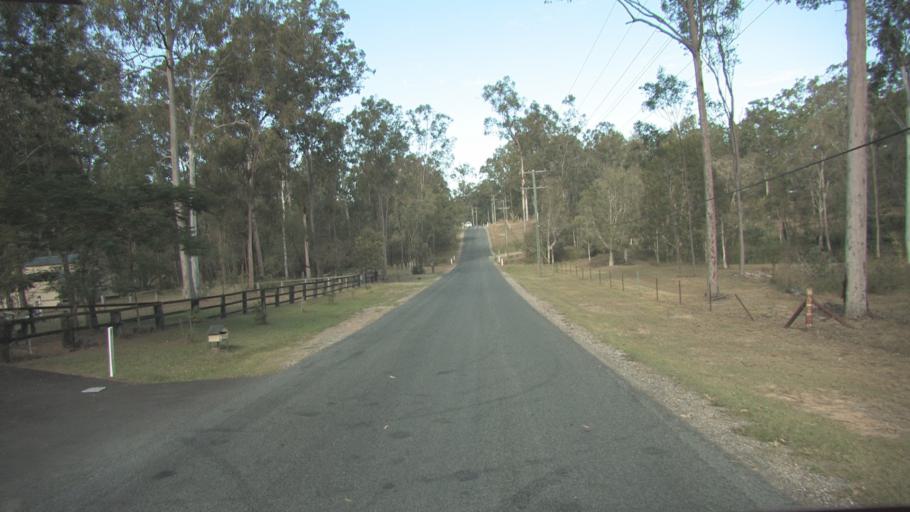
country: AU
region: Queensland
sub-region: Logan
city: North Maclean
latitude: -27.7729
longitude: 152.9654
